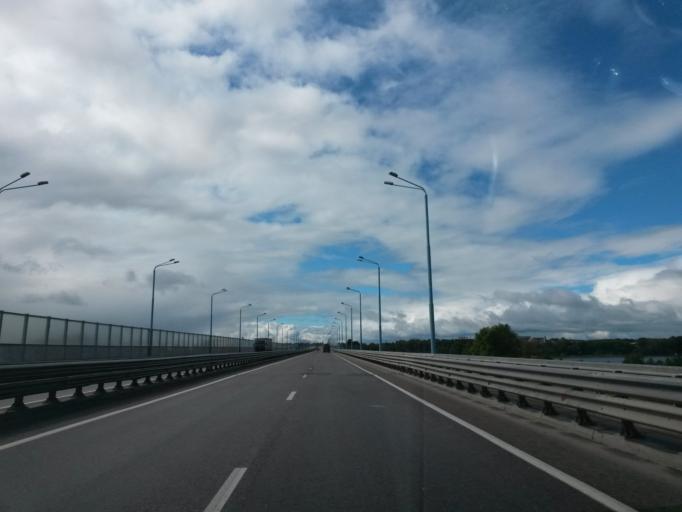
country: RU
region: Jaroslavl
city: Yaroslavl
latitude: 57.6782
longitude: 39.8660
